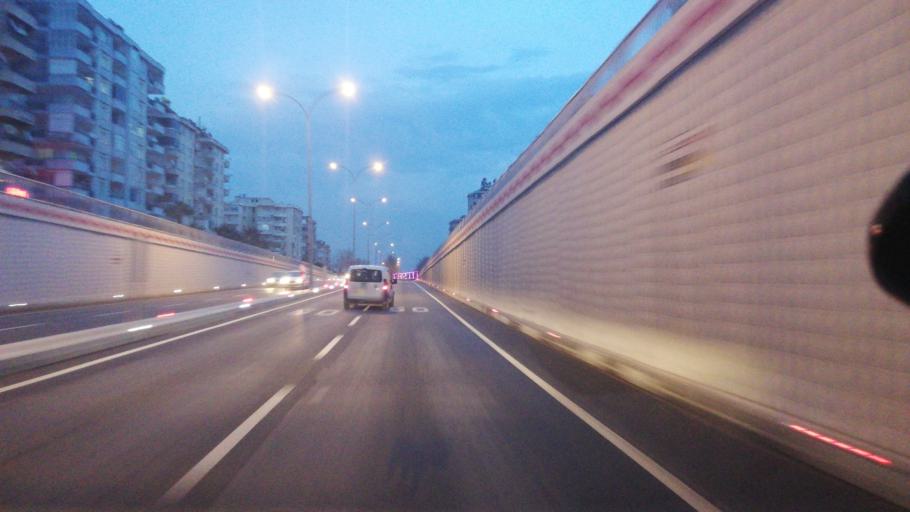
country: TR
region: Kahramanmaras
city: Kahramanmaras
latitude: 37.5844
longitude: 36.9062
